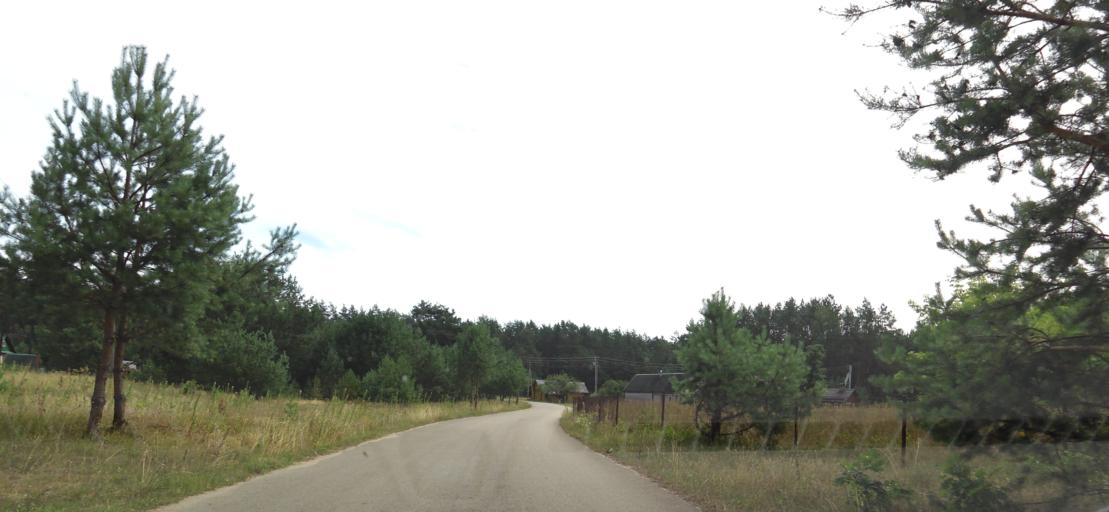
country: LT
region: Vilnius County
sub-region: Trakai
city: Rudiskes
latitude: 54.3517
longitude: 24.8436
